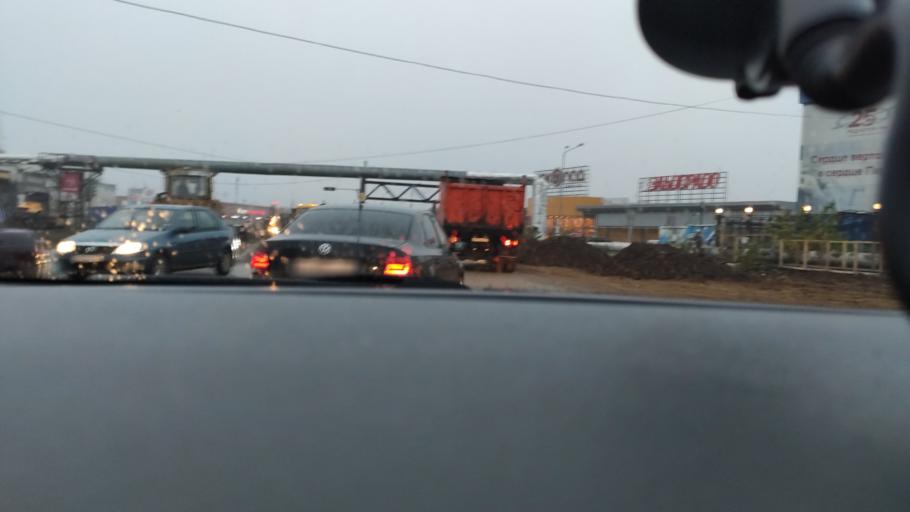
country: RU
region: Perm
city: Froly
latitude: 57.9636
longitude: 56.2637
